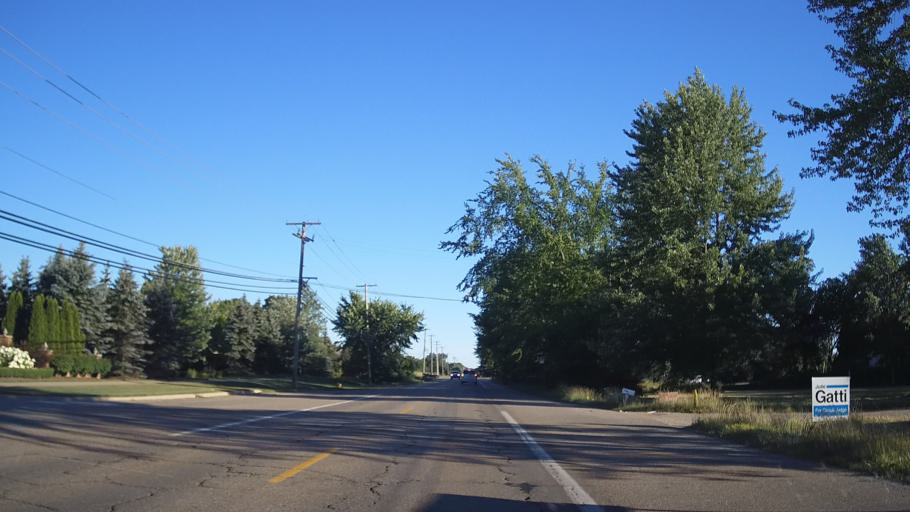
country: US
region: Michigan
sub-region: Macomb County
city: Shelby
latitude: 42.7129
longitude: -82.9596
